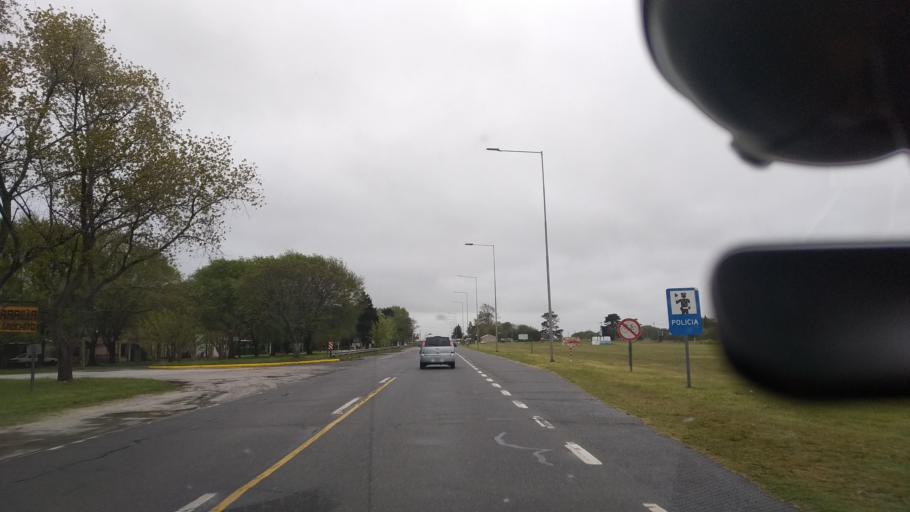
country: AR
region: Buenos Aires
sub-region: Partido de Castelli
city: Castelli
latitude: -35.9775
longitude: -57.4495
